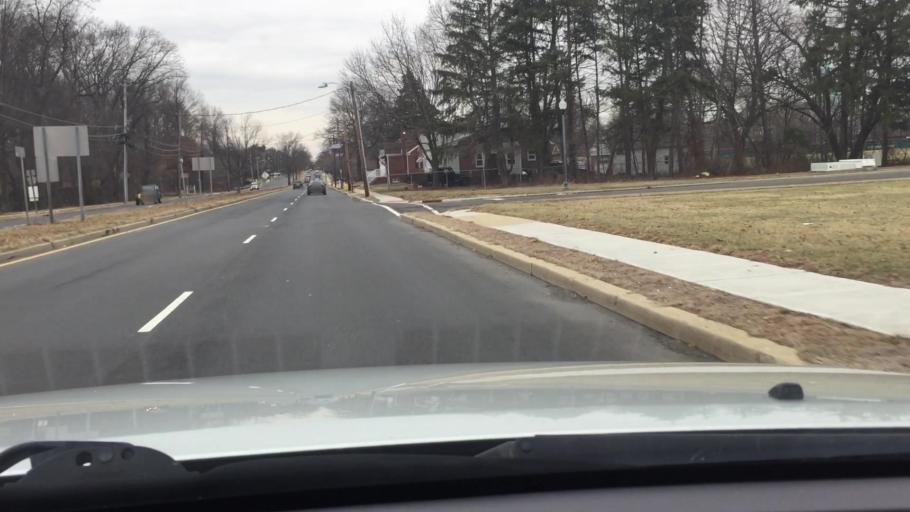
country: US
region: New Jersey
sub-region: Middlesex County
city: Old Bridge
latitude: 40.4207
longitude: -74.3892
